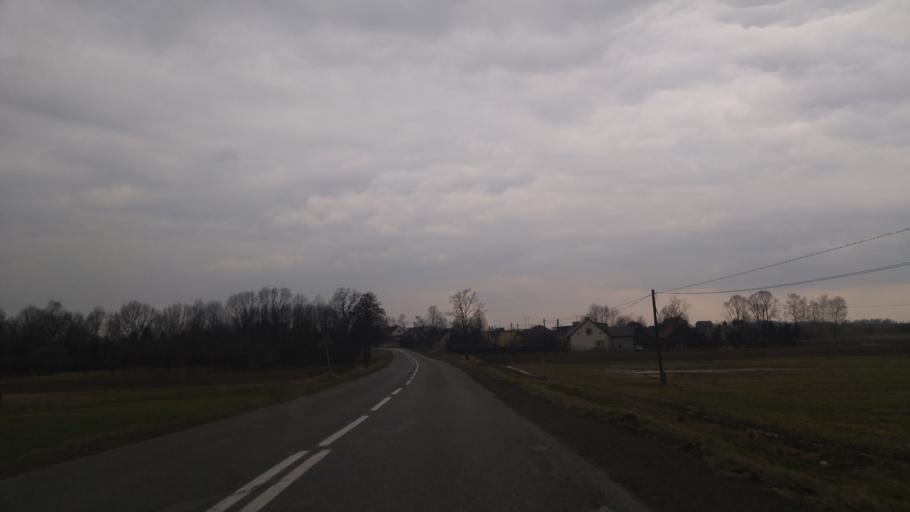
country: PL
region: Silesian Voivodeship
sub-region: Powiat cieszynski
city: Chybie
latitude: 49.9413
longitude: 18.8185
